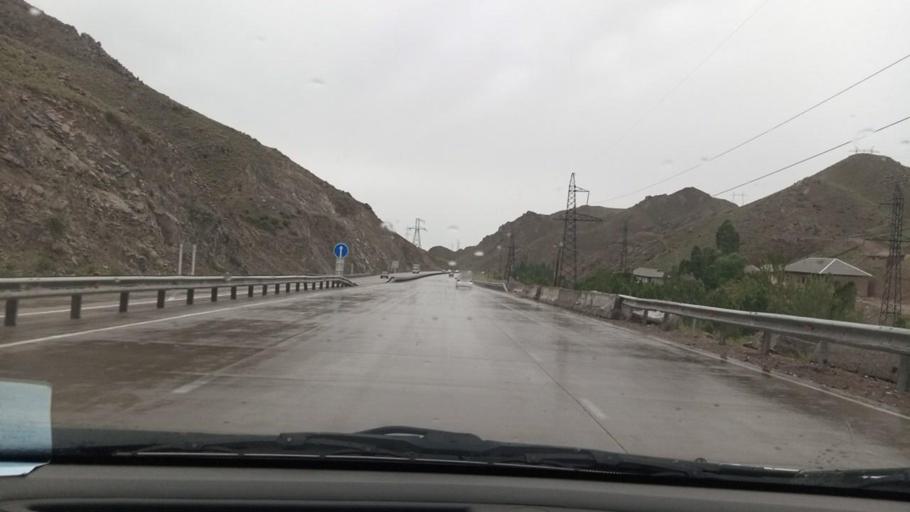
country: TJ
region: Viloyati Sughd
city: Shaydon
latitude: 40.9673
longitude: 70.6568
